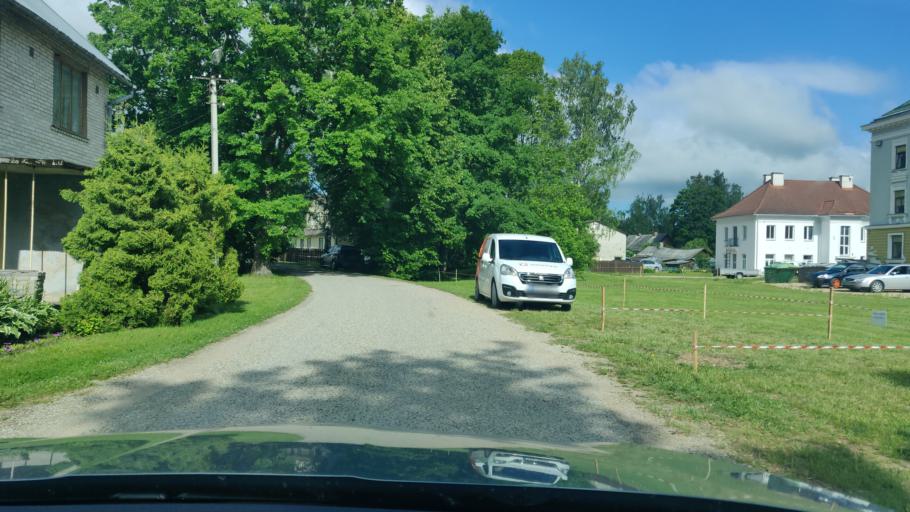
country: EE
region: Vorumaa
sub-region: Voru linn
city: Voru
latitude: 57.7310
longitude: 27.2820
